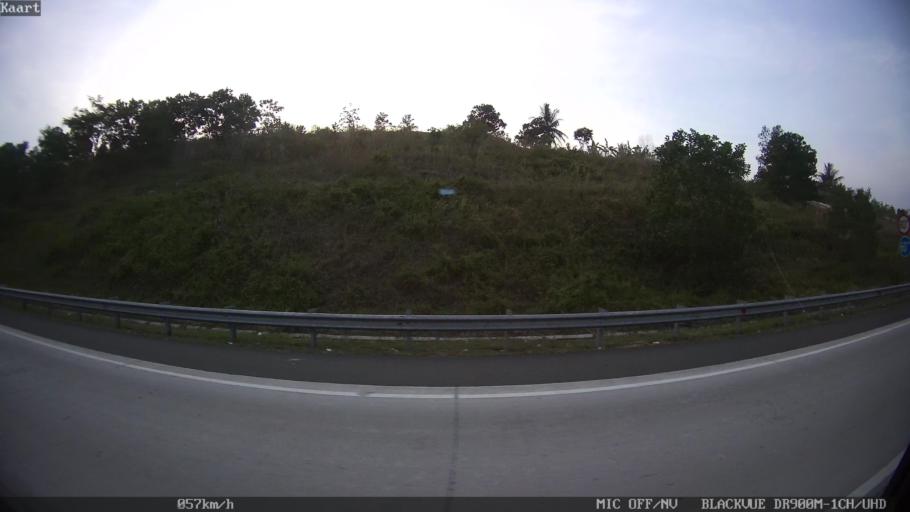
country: ID
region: Lampung
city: Penengahan
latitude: -5.8401
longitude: 105.7289
